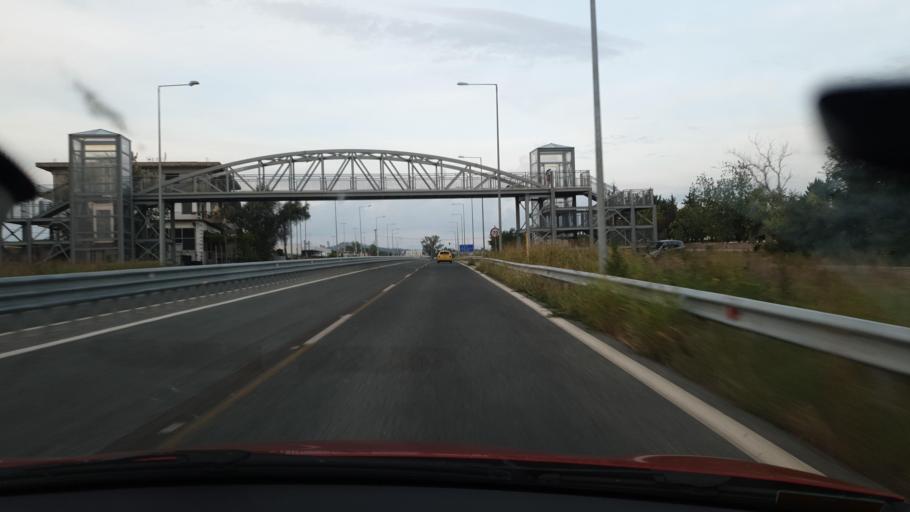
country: GR
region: Central Macedonia
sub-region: Nomos Kilkis
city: Kristoni
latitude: 40.9766
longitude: 22.8595
